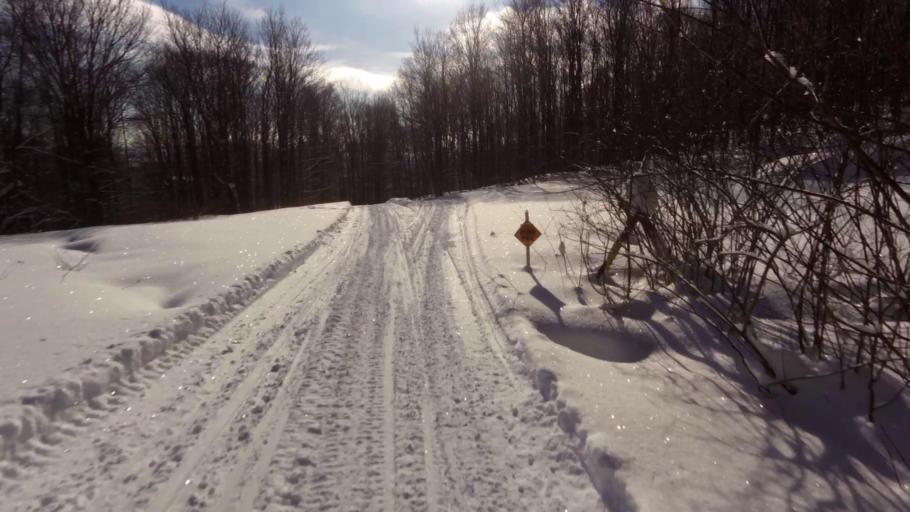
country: US
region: New York
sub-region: Chautauqua County
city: Falconer
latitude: 42.2743
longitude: -79.1222
